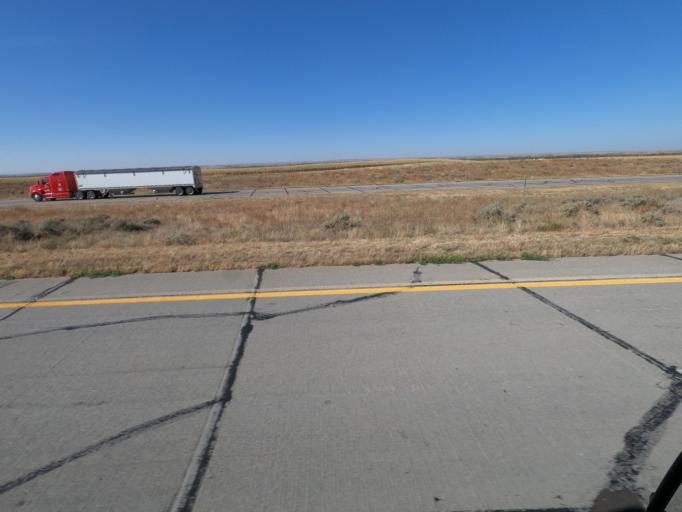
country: US
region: Nebraska
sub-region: Cheyenne County
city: Sidney
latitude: 40.8149
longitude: -102.8330
